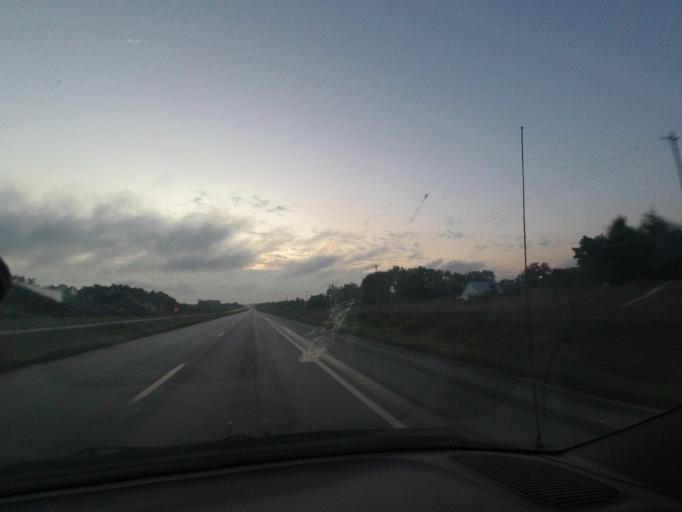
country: US
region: Missouri
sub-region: Linn County
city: Marceline
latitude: 39.7620
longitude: -92.9990
